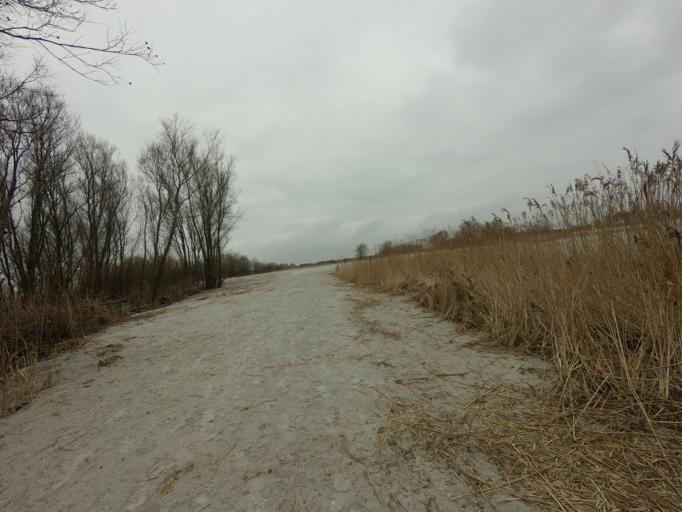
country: NL
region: Friesland
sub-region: Sudwest Fryslan
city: Makkum
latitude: 53.0536
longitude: 5.3732
